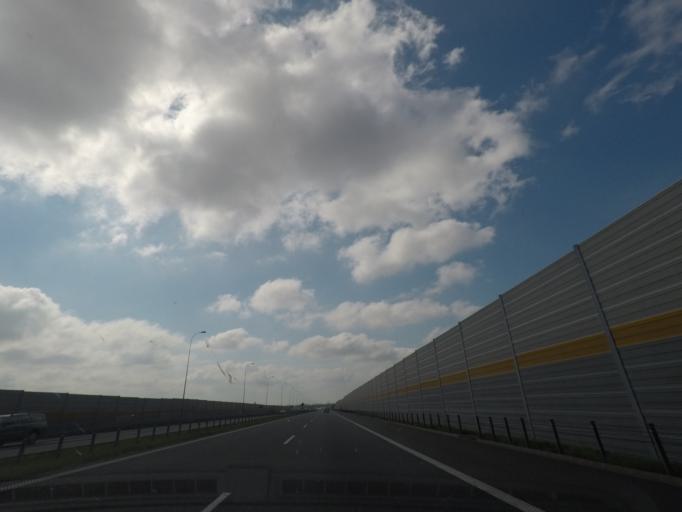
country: PL
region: Kujawsko-Pomorskie
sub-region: Powiat torunski
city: Lubicz Dolny
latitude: 53.0986
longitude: 18.7491
